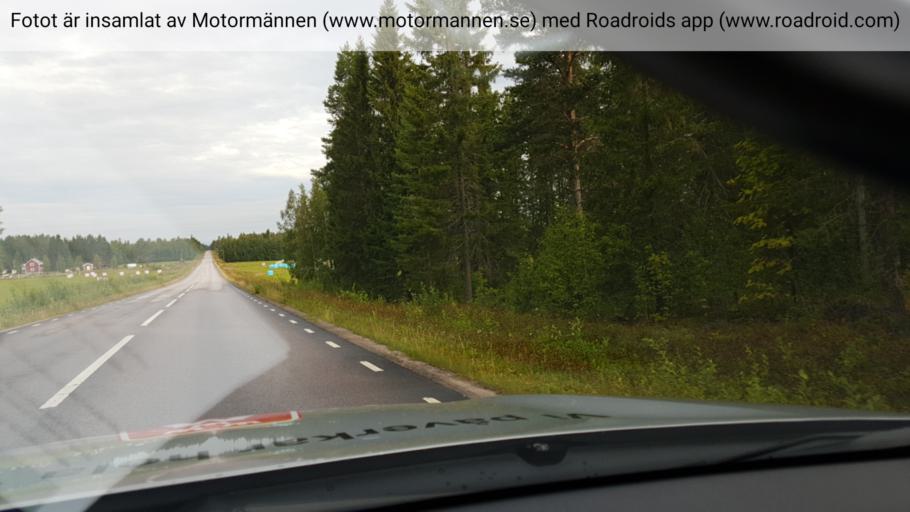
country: SE
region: Norrbotten
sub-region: Lulea Kommun
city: Sodra Sunderbyn
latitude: 65.6079
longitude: 21.9615
